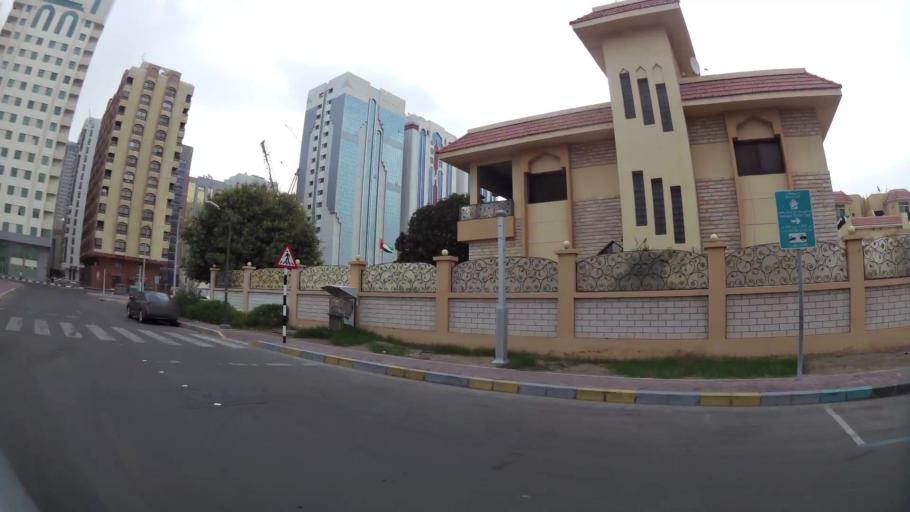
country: AE
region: Abu Dhabi
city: Abu Dhabi
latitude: 24.4682
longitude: 54.3702
